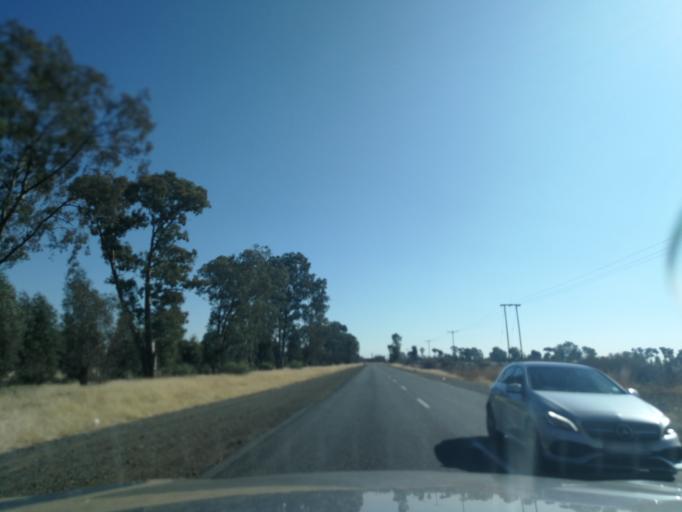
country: ZA
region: Orange Free State
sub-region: Fezile Dabi District Municipality
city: Kroonstad
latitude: -27.6290
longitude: 27.2156
